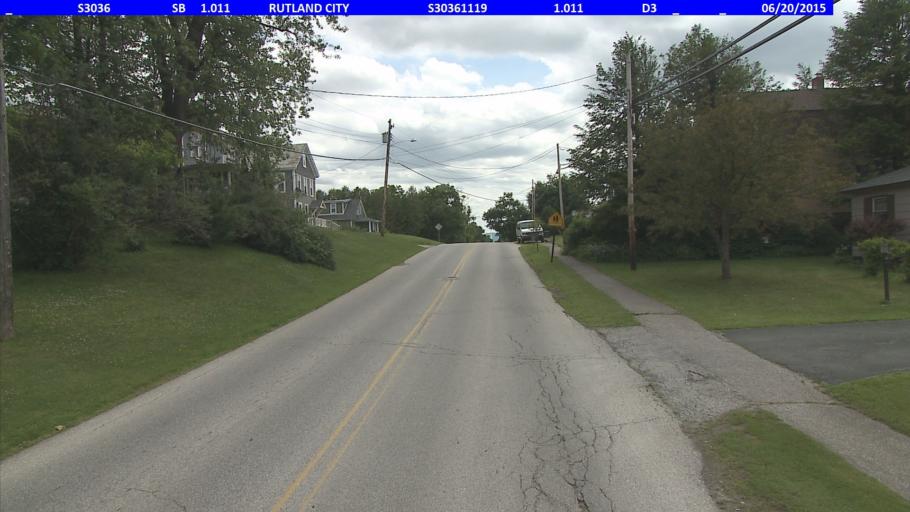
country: US
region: Vermont
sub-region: Rutland County
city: Rutland
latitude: 43.6228
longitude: -72.9784
